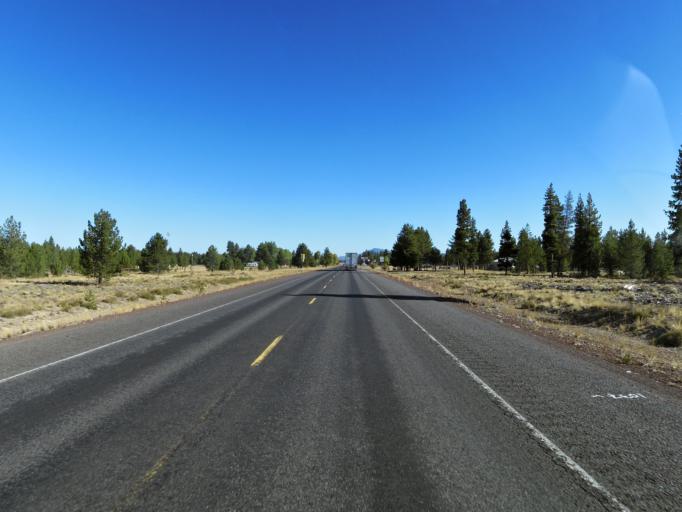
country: US
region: Oregon
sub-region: Deschutes County
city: La Pine
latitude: 43.1300
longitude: -121.8047
